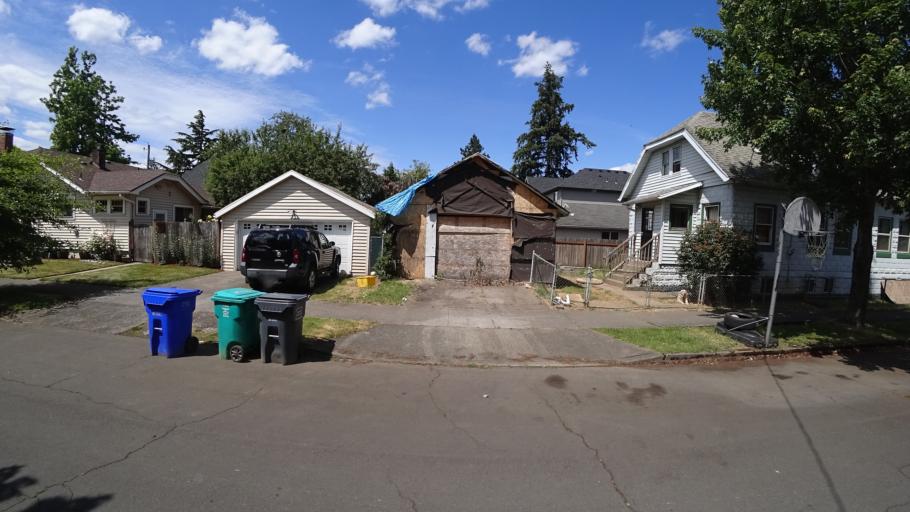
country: US
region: Oregon
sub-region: Multnomah County
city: Portland
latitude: 45.5866
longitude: -122.7189
